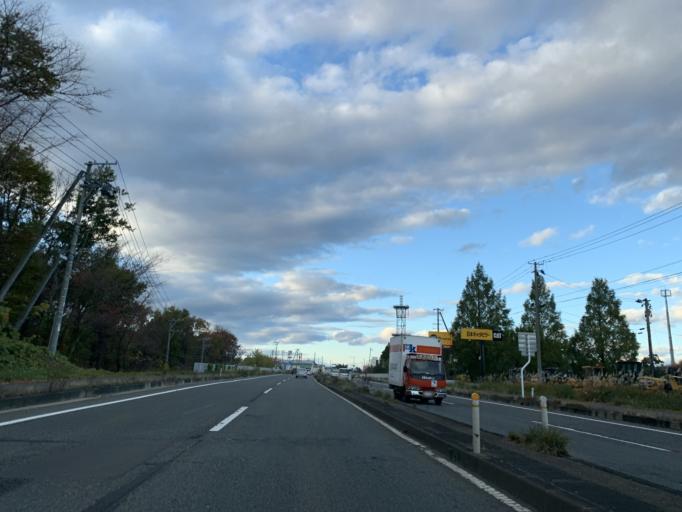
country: JP
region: Iwate
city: Kitakami
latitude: 39.2590
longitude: 141.0992
